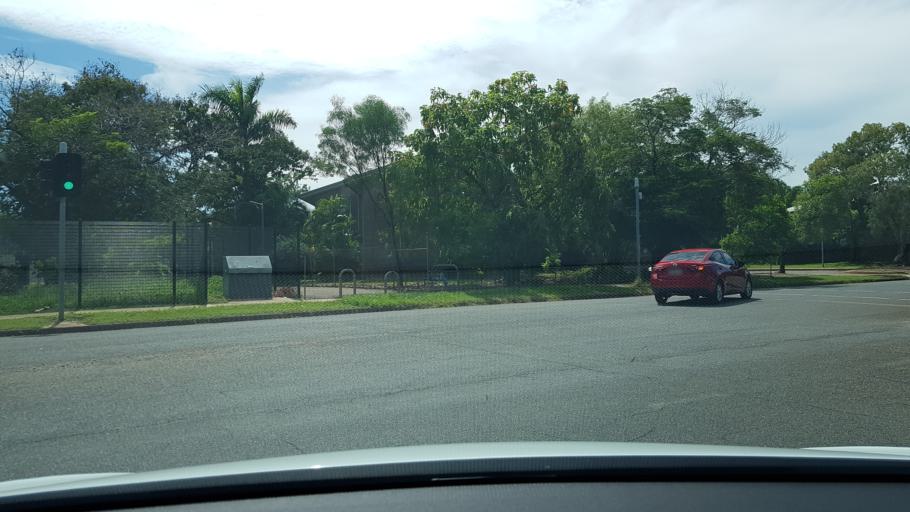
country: AU
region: Northern Territory
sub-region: Darwin
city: Leanyer
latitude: -12.3699
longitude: 130.8833
